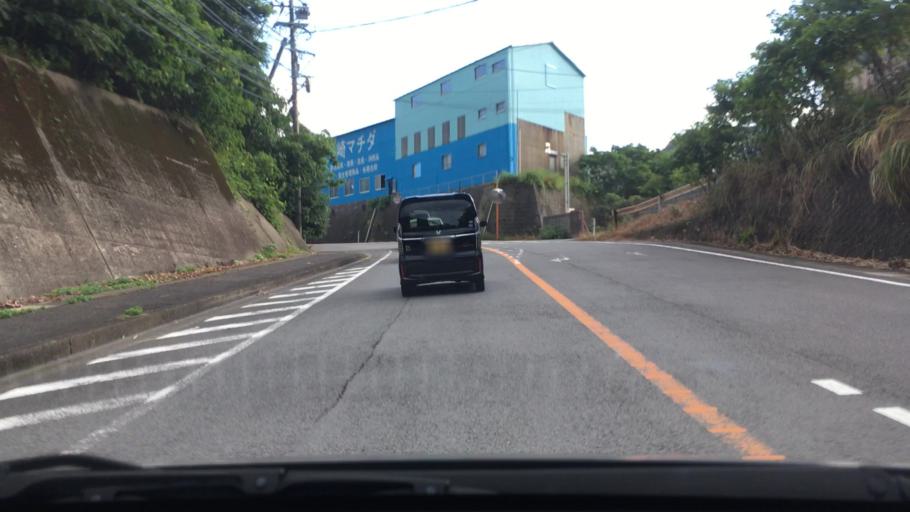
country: JP
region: Nagasaki
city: Togitsu
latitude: 32.8128
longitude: 129.8090
